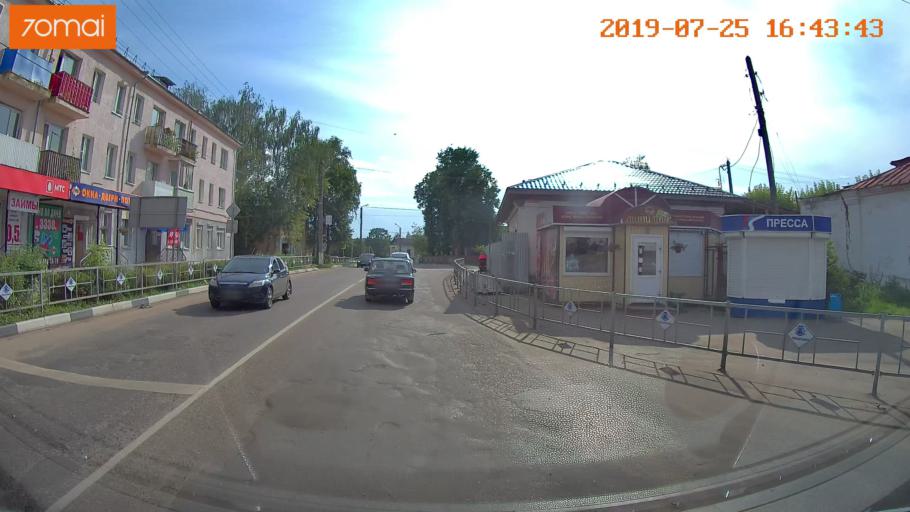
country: RU
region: Ivanovo
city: Privolzhsk
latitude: 57.3800
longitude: 41.2821
